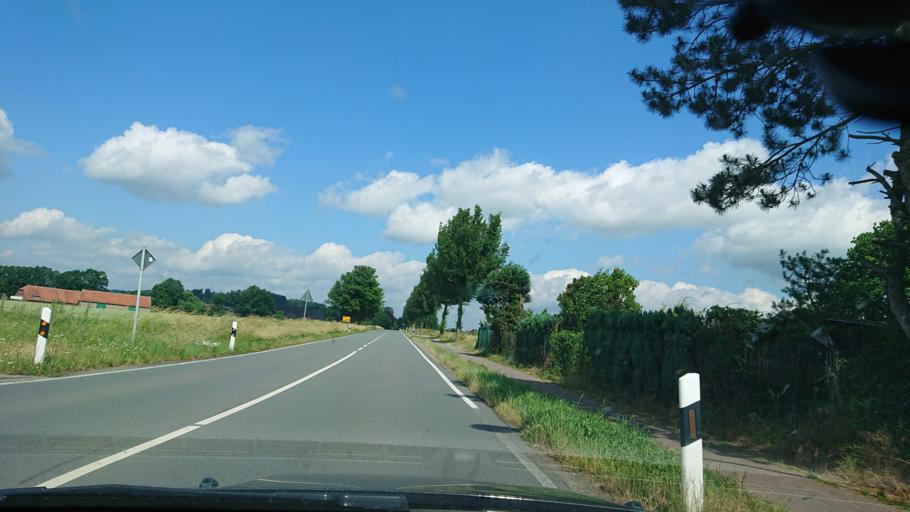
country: DE
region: North Rhine-Westphalia
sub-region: Regierungsbezirk Detmold
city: Rodinghausen
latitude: 52.2098
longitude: 8.4431
